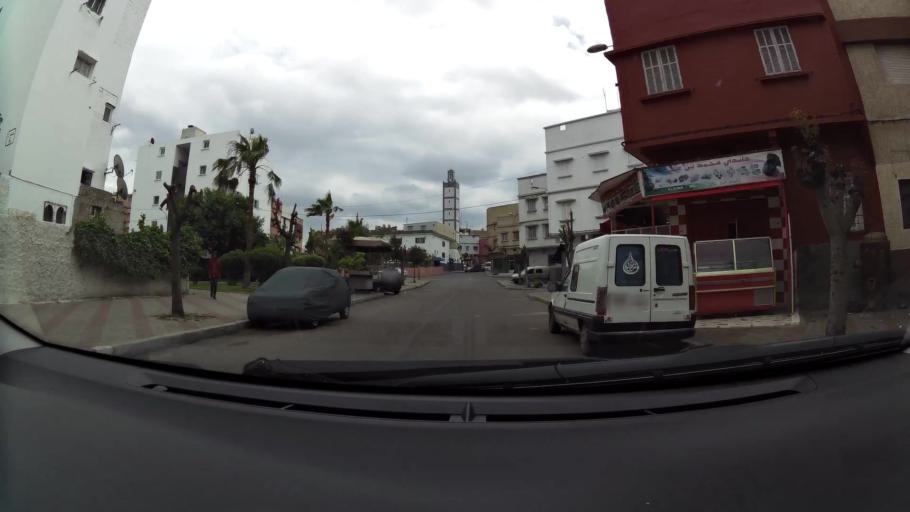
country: MA
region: Grand Casablanca
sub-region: Casablanca
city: Casablanca
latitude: 33.5832
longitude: -7.5647
